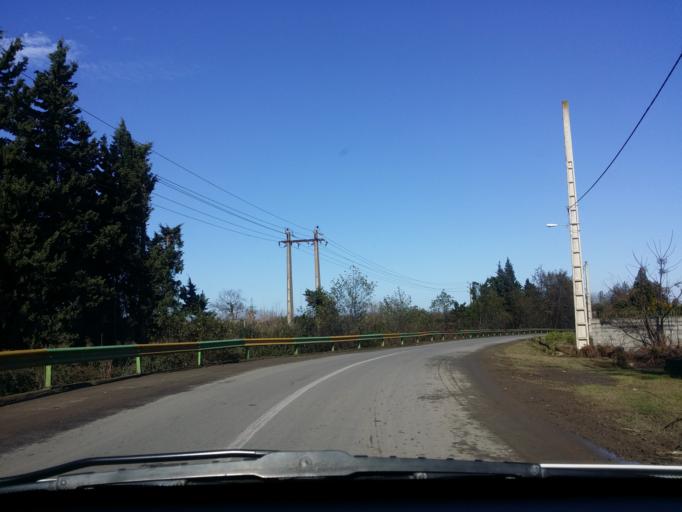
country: IR
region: Mazandaran
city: Chalus
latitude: 36.6824
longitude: 51.3132
